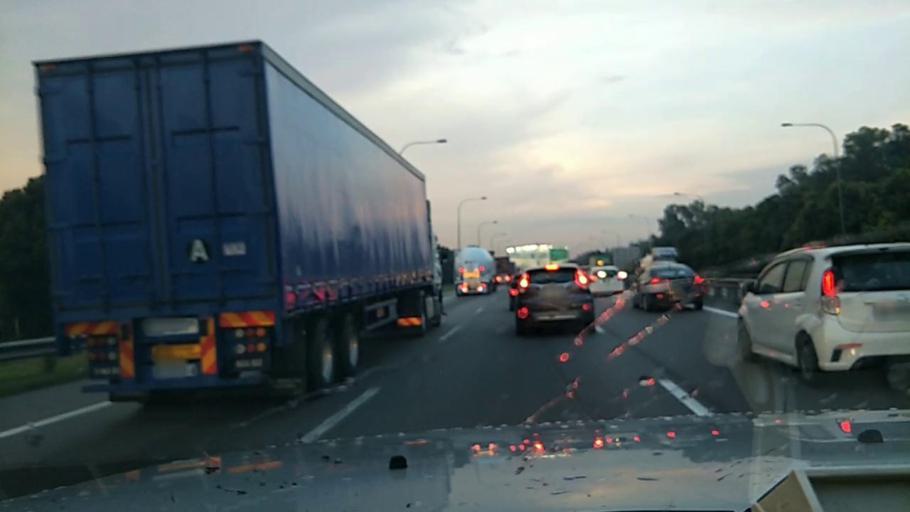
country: MY
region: Putrajaya
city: Putrajaya
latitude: 2.9303
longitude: 101.6000
